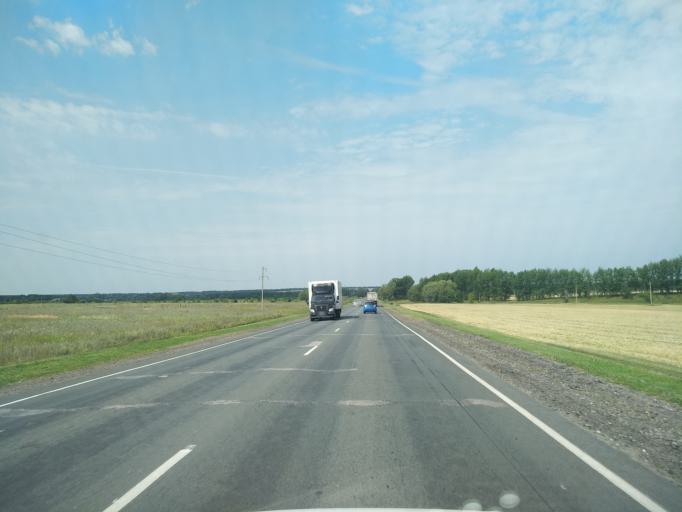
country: RU
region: Voronezj
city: Orlovo
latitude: 51.6800
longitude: 39.6185
